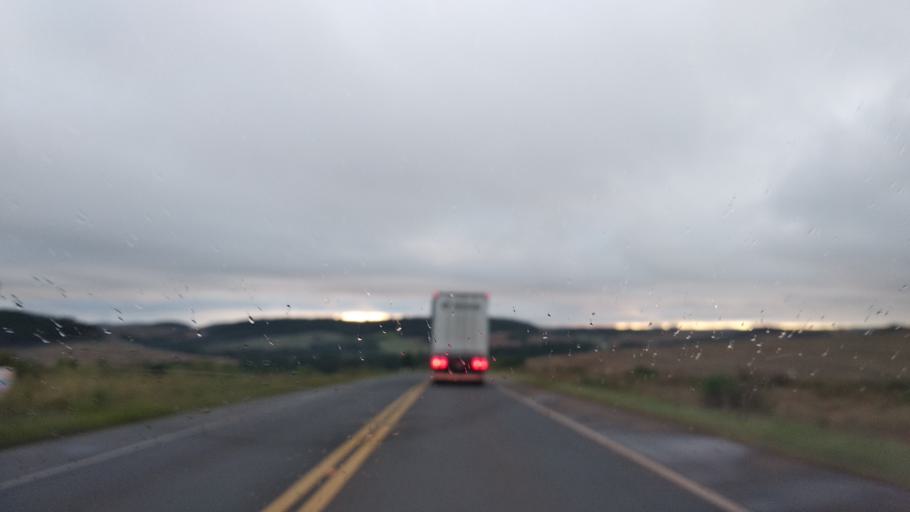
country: BR
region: Santa Catarina
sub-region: Campos Novos
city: Campos Novos
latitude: -27.3749
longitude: -51.0743
